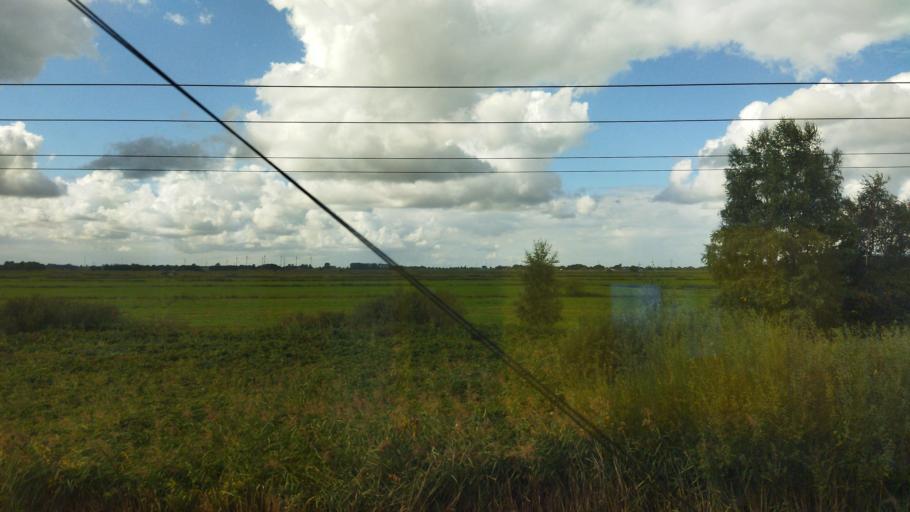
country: DE
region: Lower Saxony
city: Leer
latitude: 53.2029
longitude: 7.4653
